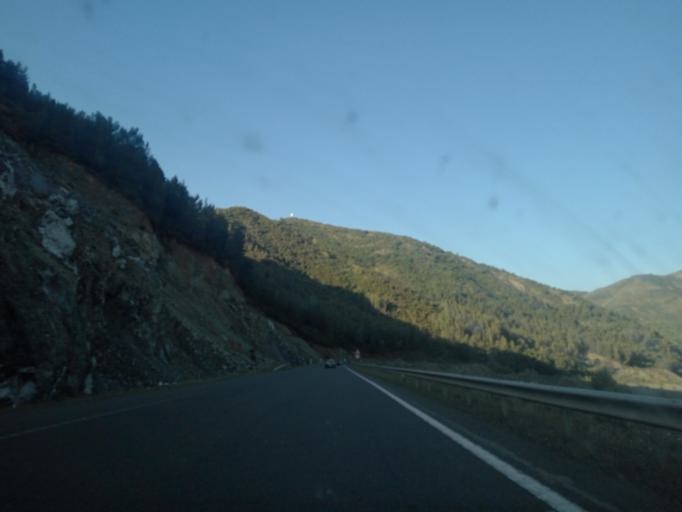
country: AL
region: Lezhe
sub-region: Rrethi i Mirdites
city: Rubik
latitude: 41.7910
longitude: 19.8002
